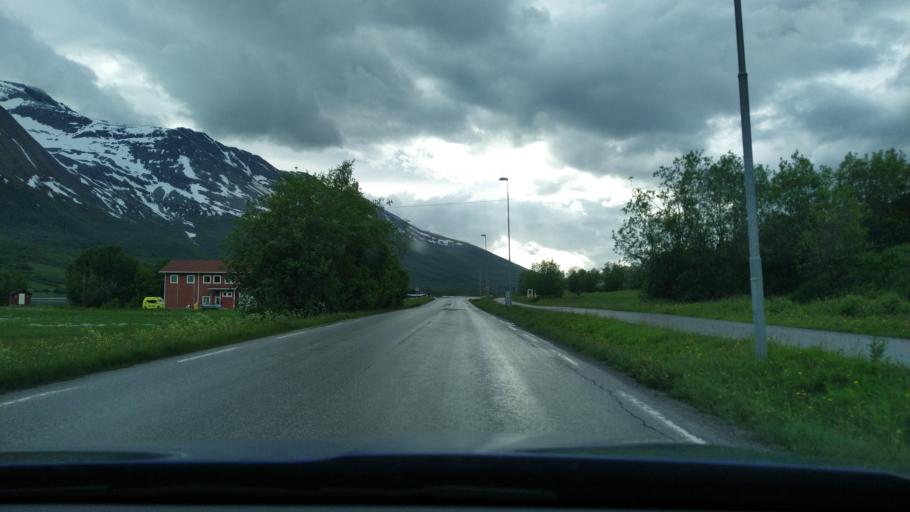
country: NO
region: Troms
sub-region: Balsfjord
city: Storsteinnes
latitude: 69.2201
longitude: 19.5432
